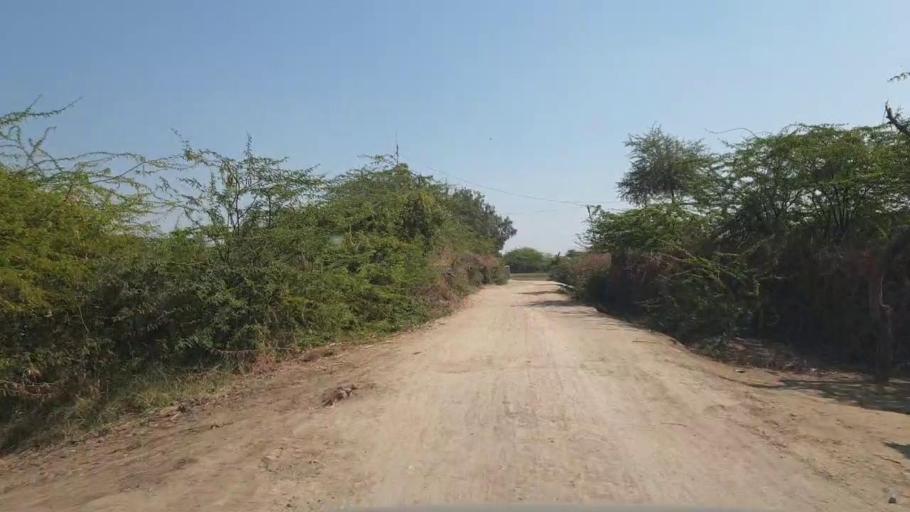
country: PK
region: Sindh
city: Digri
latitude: 25.0914
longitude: 69.2323
